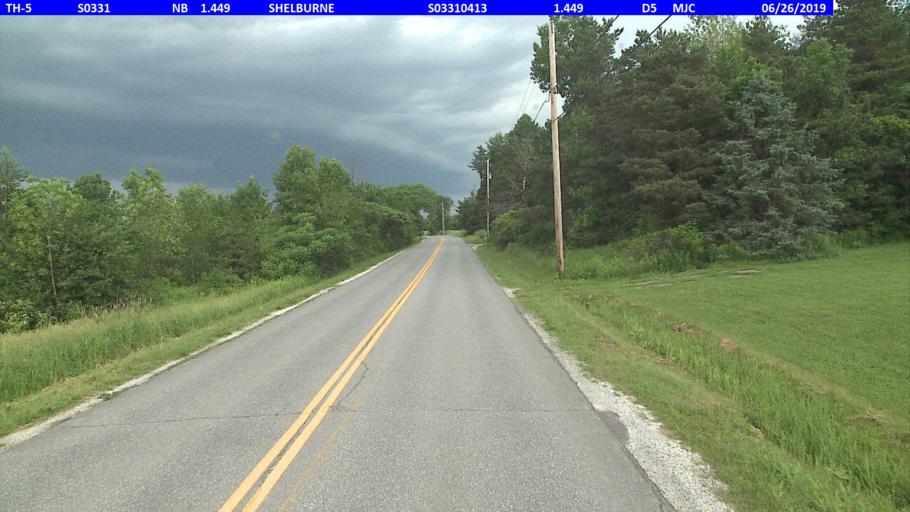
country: US
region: Vermont
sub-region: Chittenden County
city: South Burlington
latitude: 44.3916
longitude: -73.1759
